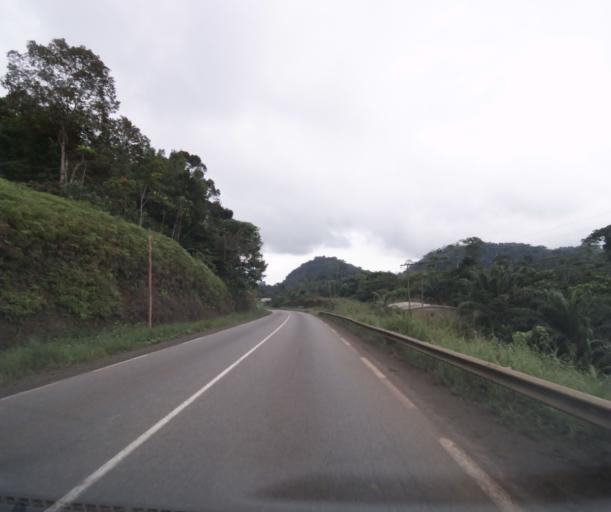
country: CM
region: Littoral
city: Edea
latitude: 3.8041
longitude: 10.2291
